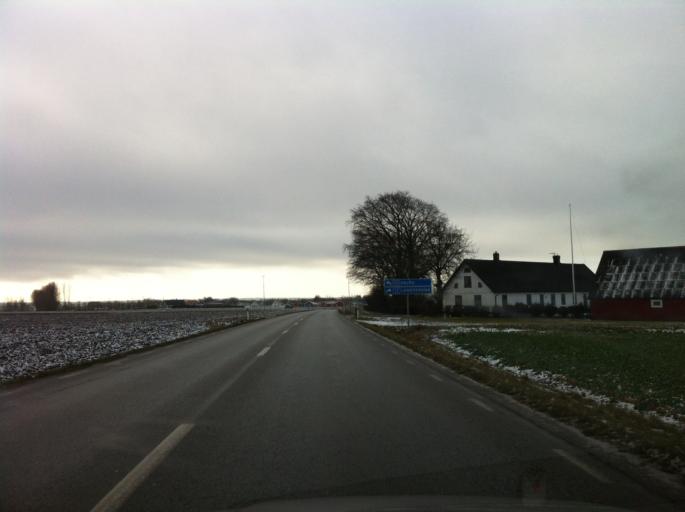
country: SE
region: Skane
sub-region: Svalovs Kommun
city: Teckomatorp
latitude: 55.8871
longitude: 13.0129
